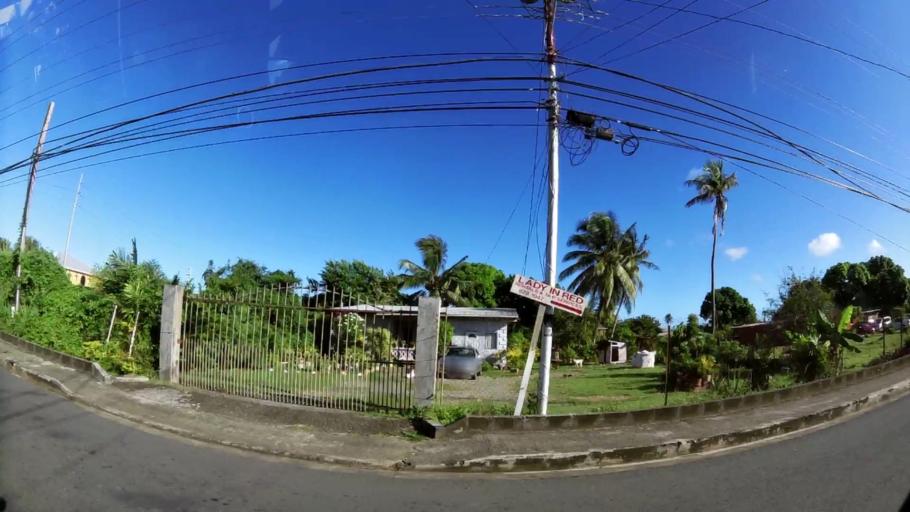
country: TT
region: Tobago
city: Scarborough
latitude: 11.1537
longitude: -60.8365
